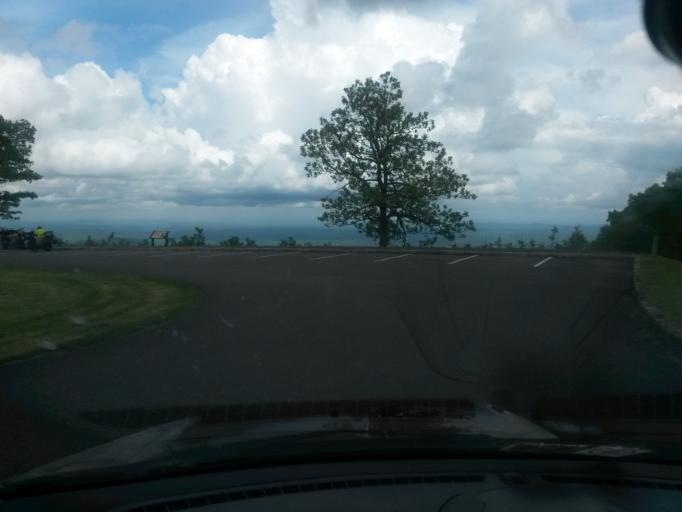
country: US
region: Virginia
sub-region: Floyd County
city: Floyd
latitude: 36.8121
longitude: -80.3463
